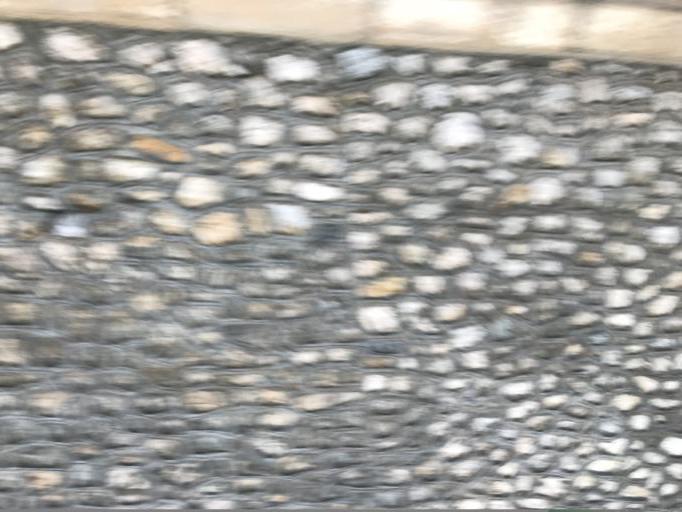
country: TR
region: Bartin
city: Amasra
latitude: 41.7333
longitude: 32.3793
